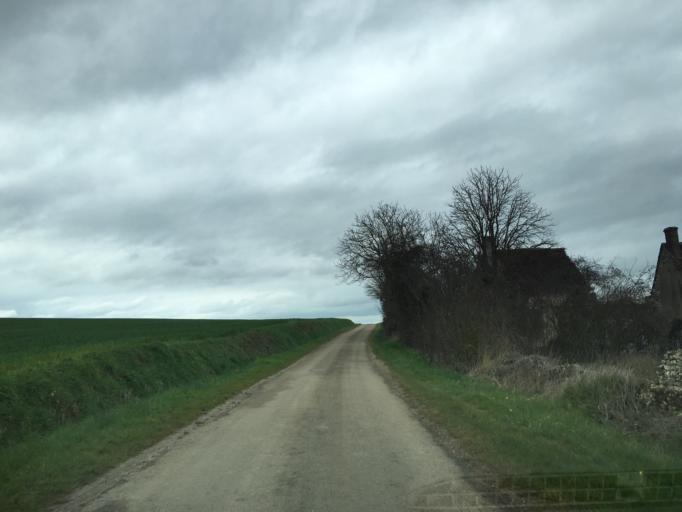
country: FR
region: Bourgogne
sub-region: Departement de l'Yonne
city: Fleury-la-Vallee
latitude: 47.8493
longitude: 3.4347
